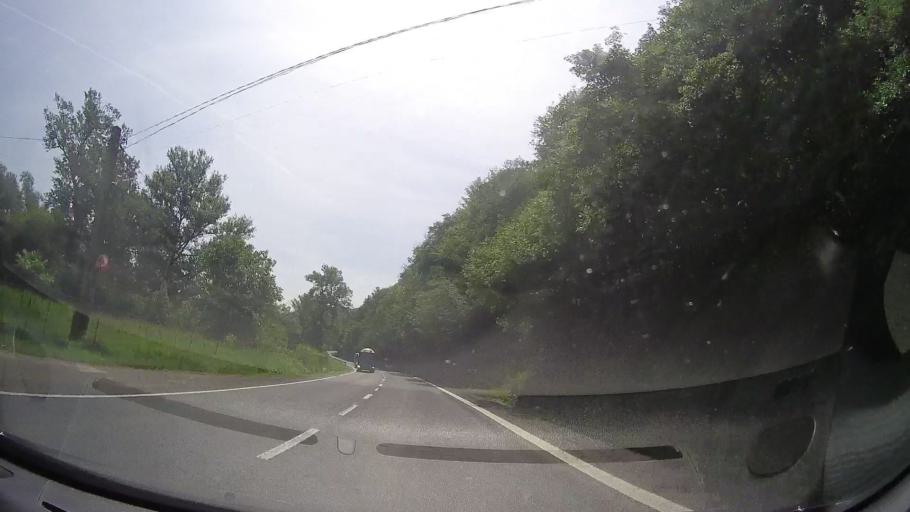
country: RO
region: Hunedoara
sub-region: Comuna Branisca
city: Branisca
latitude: 45.9099
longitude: 22.7707
